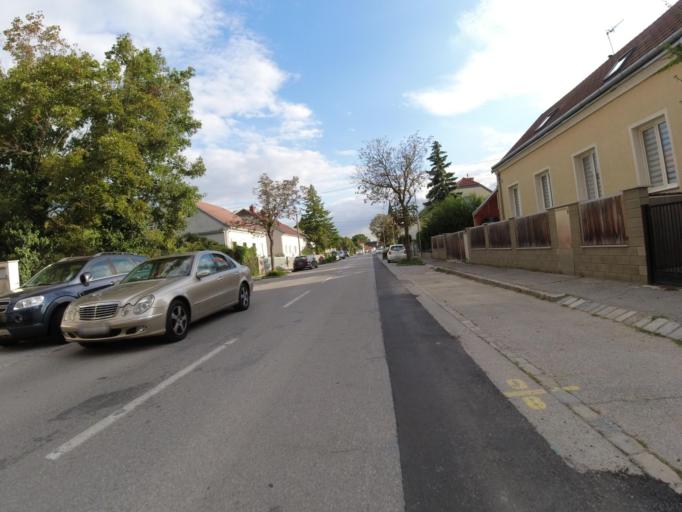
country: AT
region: Lower Austria
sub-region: Politischer Bezirk Baden
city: Pfaffstatten
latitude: 48.0088
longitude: 16.2711
